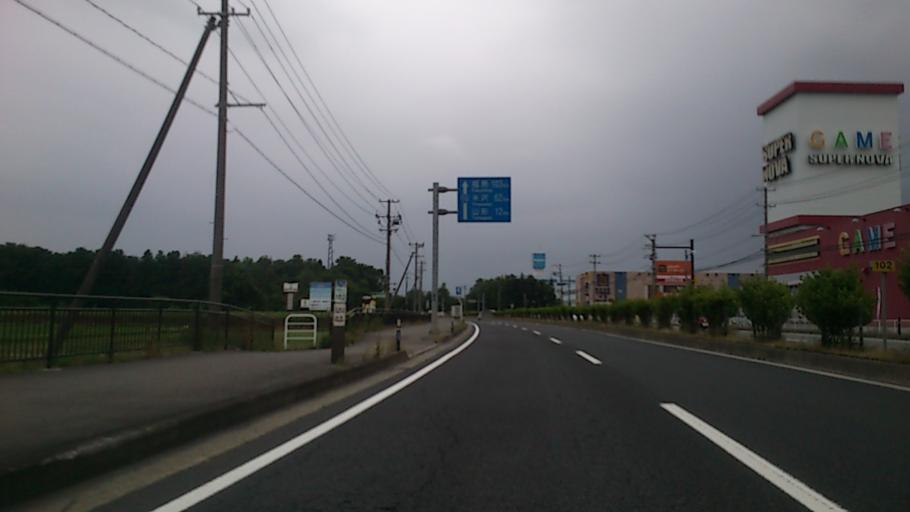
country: JP
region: Yamagata
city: Tendo
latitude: 38.3431
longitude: 140.3753
